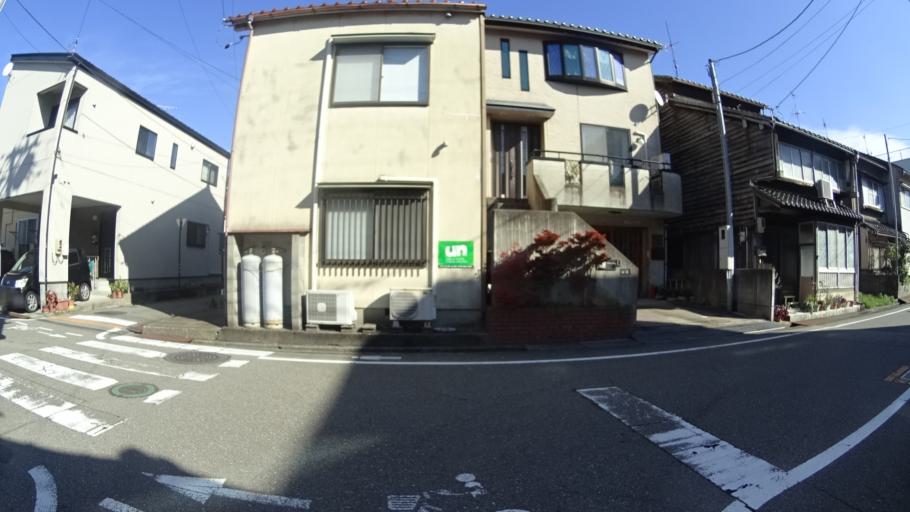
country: JP
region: Ishikawa
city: Kanazawa-shi
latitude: 36.5752
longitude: 136.6629
